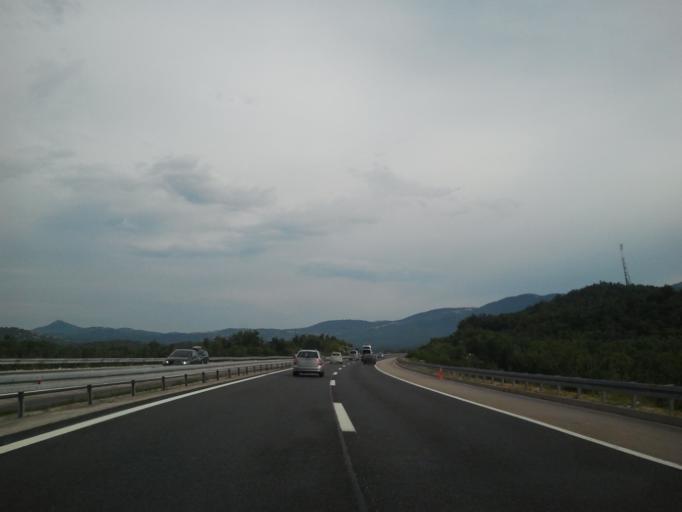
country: HR
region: Zadarska
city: Obrovac
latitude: 44.3277
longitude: 15.6720
